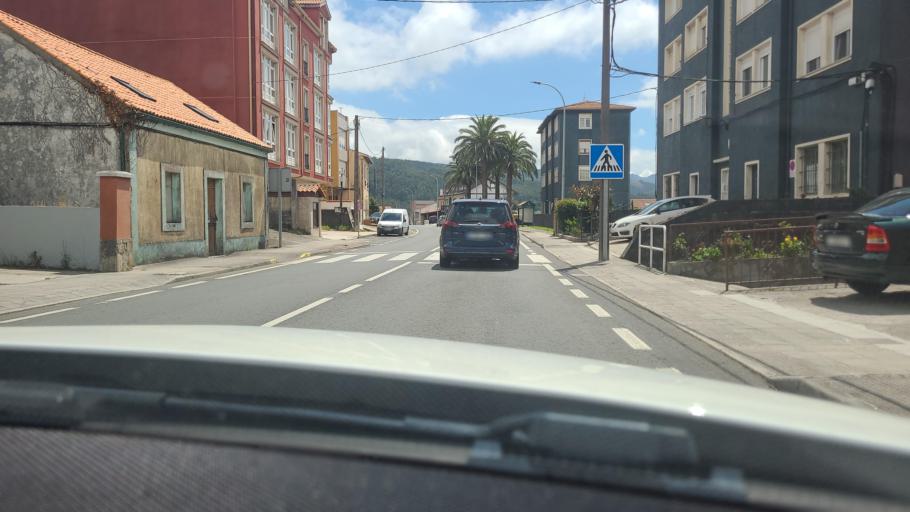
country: ES
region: Galicia
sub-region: Provincia da Coruna
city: Cee
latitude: 42.9487
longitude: -9.1823
